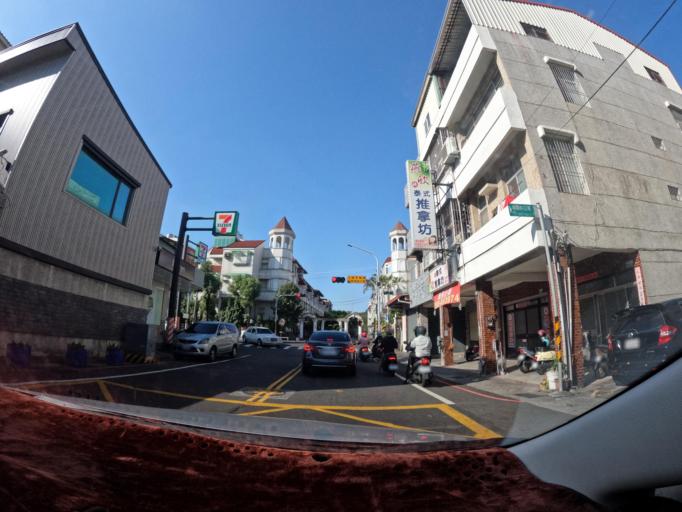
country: TW
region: Taiwan
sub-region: Tainan
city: Tainan
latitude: 23.0330
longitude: 120.2515
